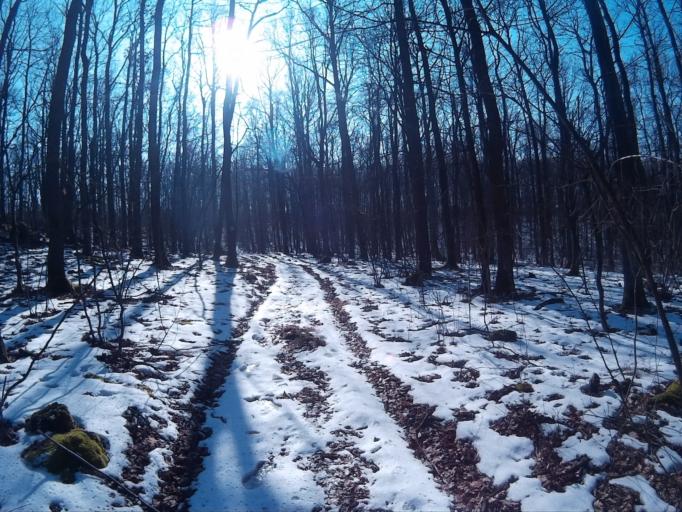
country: HU
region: Nograd
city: Paszto
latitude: 47.9808
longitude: 19.6548
